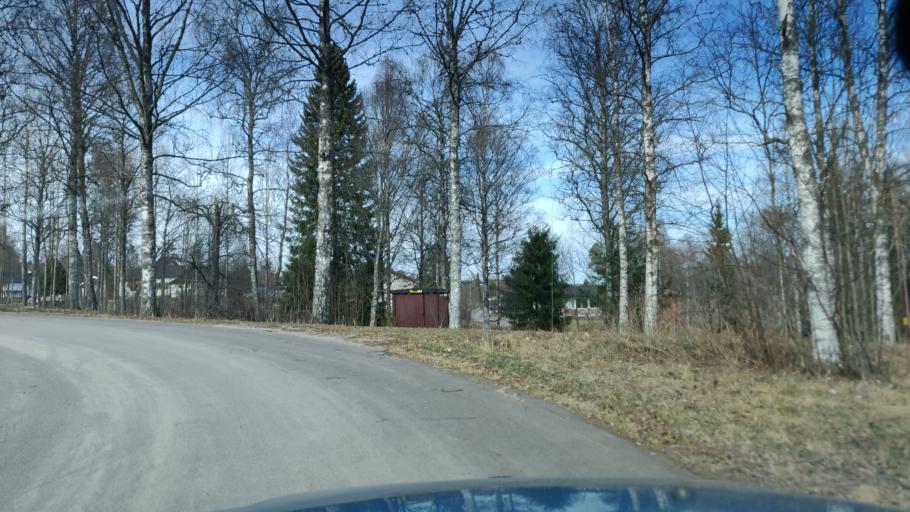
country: SE
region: Vaermland
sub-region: Hagfors Kommun
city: Hagfors
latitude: 60.0229
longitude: 13.6250
